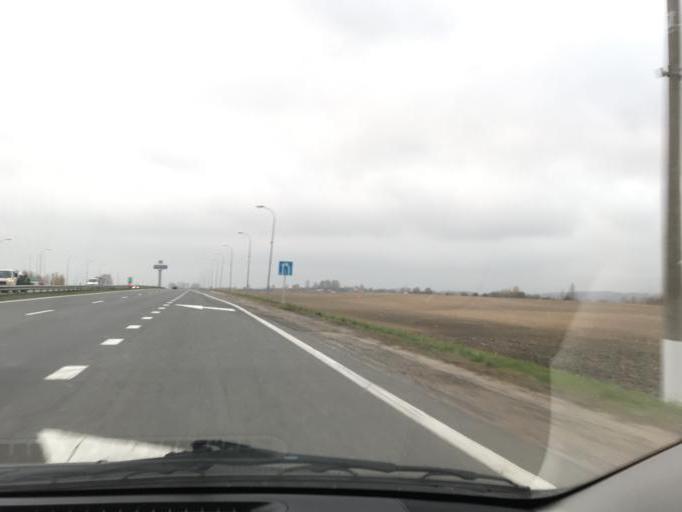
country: BY
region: Vitebsk
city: Vitebsk
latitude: 55.1531
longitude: 30.1324
